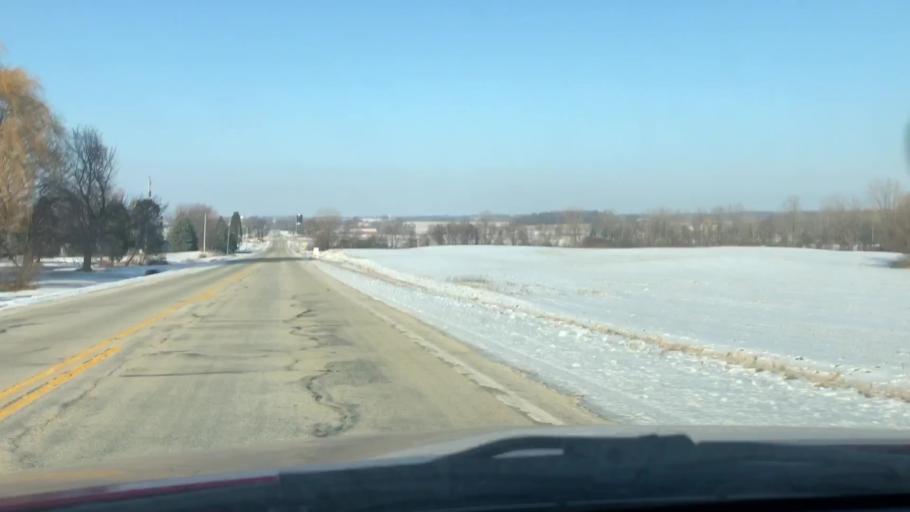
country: US
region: Wisconsin
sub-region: Outagamie County
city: Kimberly
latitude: 44.3797
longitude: -88.3748
